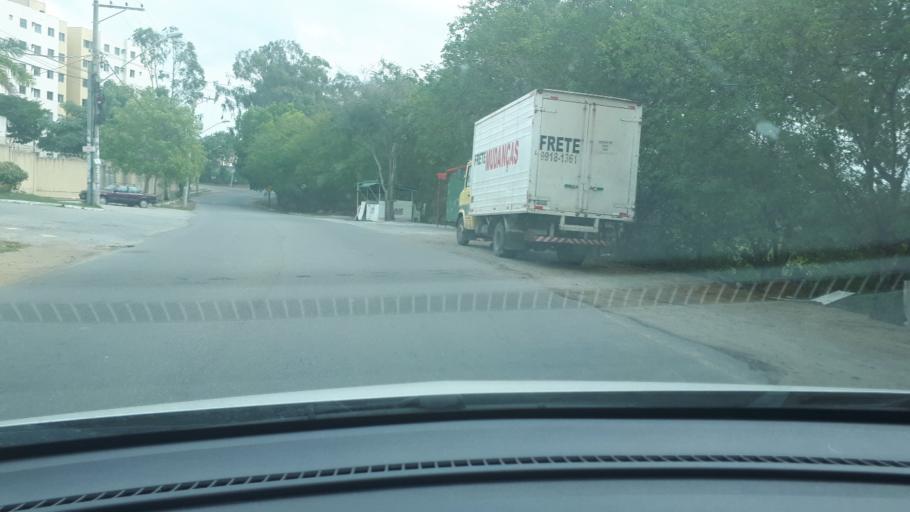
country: BR
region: Espirito Santo
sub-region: Serra
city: Serra
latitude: -20.1463
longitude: -40.1968
